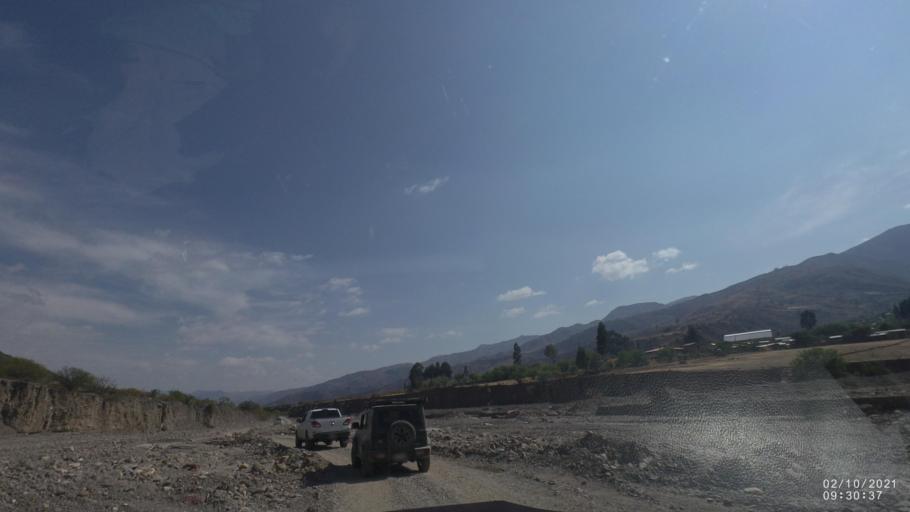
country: BO
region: Cochabamba
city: Irpa Irpa
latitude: -17.8512
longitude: -66.3186
